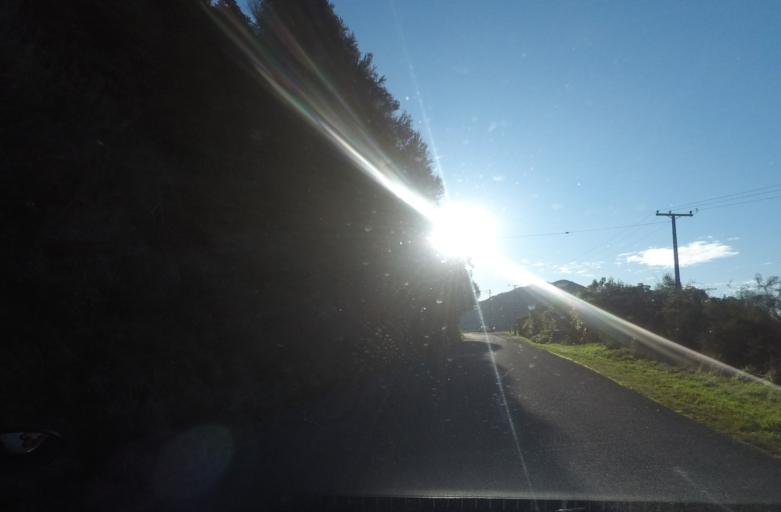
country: NZ
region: Marlborough
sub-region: Marlborough District
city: Picton
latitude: -41.2690
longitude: 173.9738
